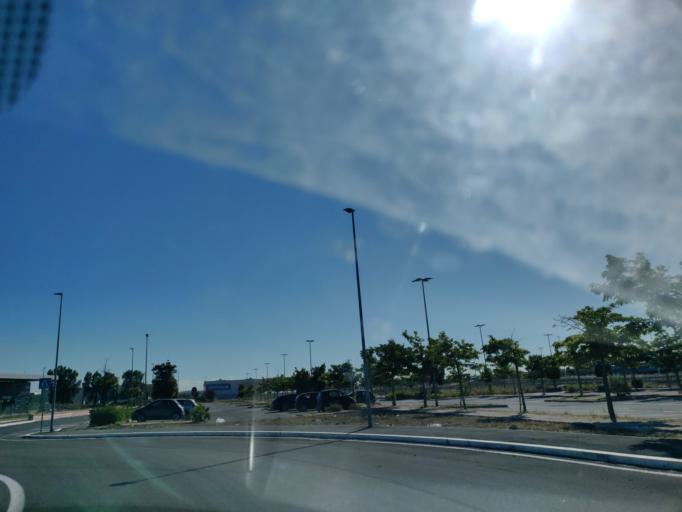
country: IT
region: Latium
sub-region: Citta metropolitana di Roma Capitale
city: Npp 23 (Parco Leonardo)
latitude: 41.8060
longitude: 12.2960
